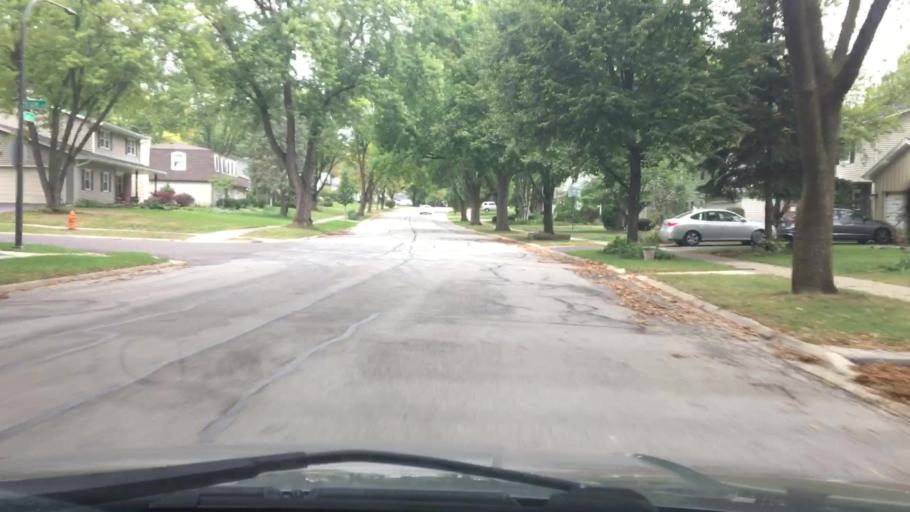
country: US
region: Illinois
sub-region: DuPage County
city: Naperville
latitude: 41.7420
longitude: -88.1353
